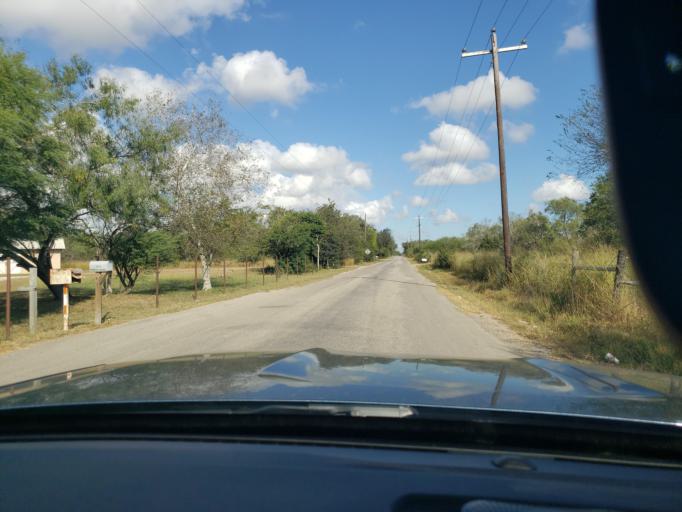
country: US
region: Texas
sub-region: Bee County
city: Beeville
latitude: 28.4415
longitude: -97.7134
